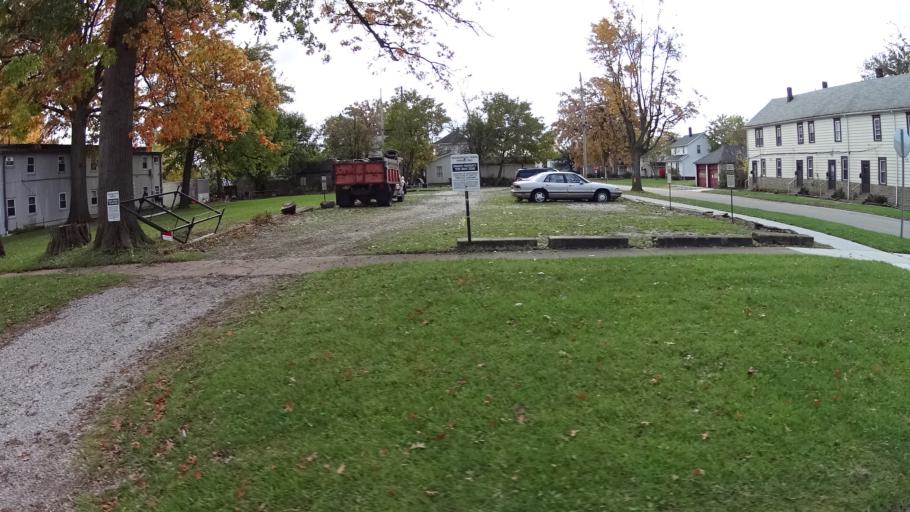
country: US
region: Ohio
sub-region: Lorain County
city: Sheffield
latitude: 41.4458
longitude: -82.1150
